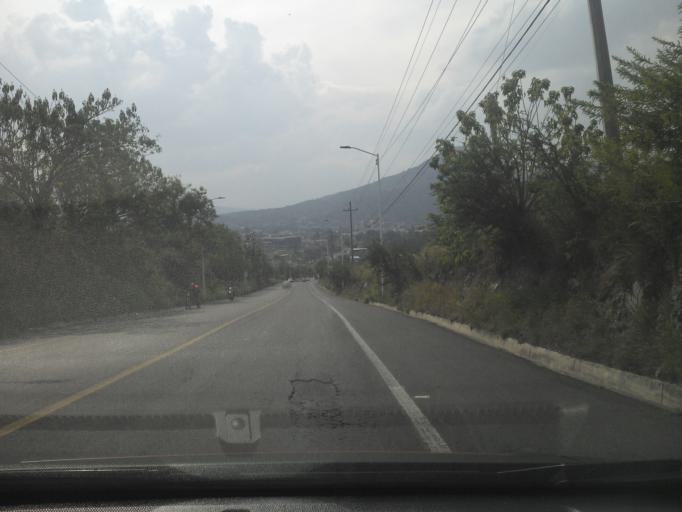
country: MX
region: Jalisco
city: Tlajomulco de Zuniga
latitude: 20.4798
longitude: -103.4337
